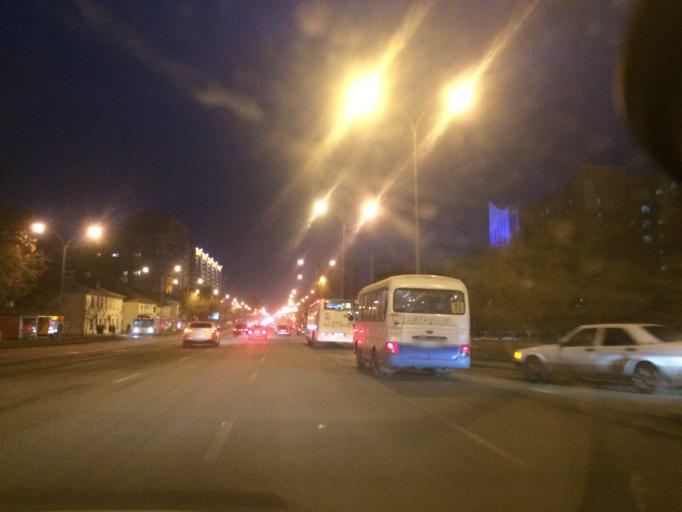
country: KZ
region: Astana Qalasy
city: Astana
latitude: 51.1754
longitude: 71.4110
